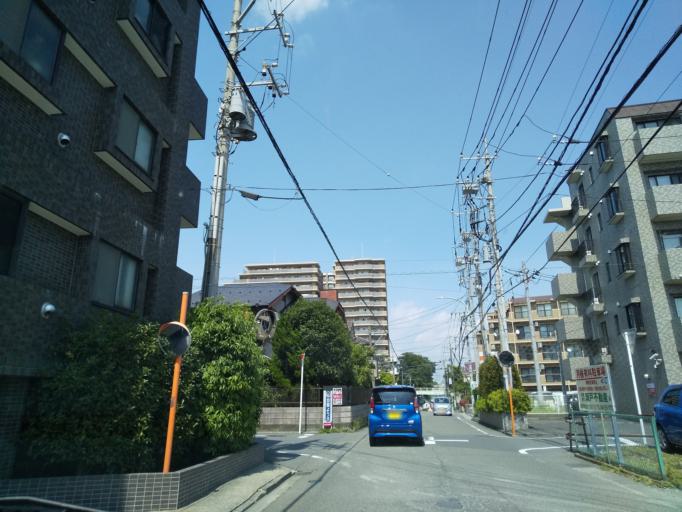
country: JP
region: Kanagawa
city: Zama
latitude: 35.5019
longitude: 139.4142
